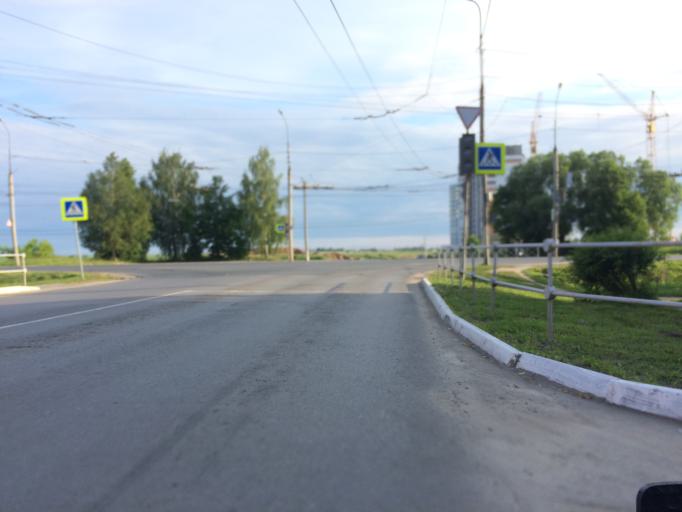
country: RU
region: Mariy-El
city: Medvedevo
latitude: 56.6388
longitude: 47.8026
